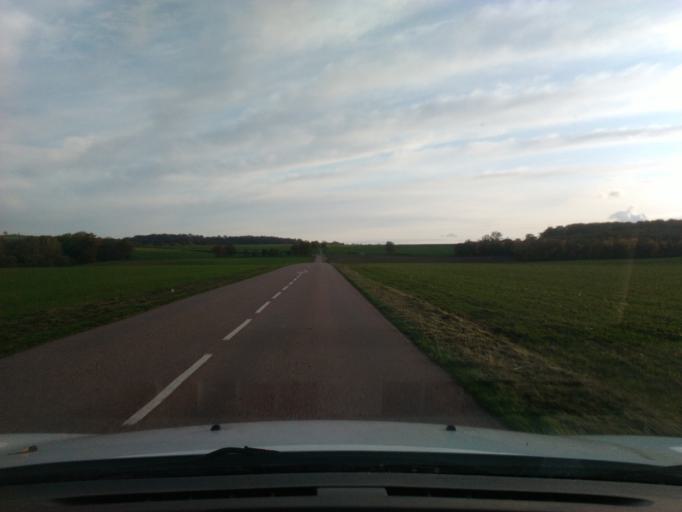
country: FR
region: Lorraine
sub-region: Departement des Vosges
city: Mirecourt
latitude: 48.2305
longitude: 6.1485
